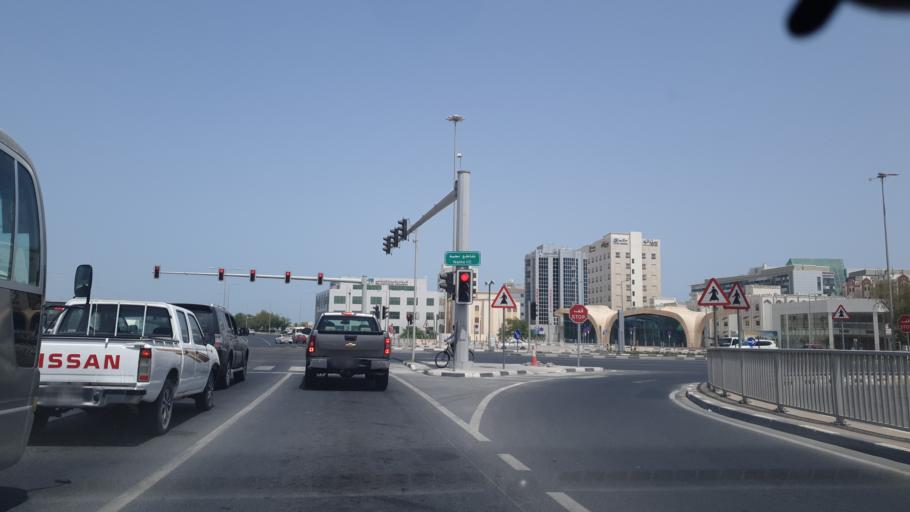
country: QA
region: Baladiyat ad Dawhah
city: Doha
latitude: 25.2676
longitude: 51.5500
